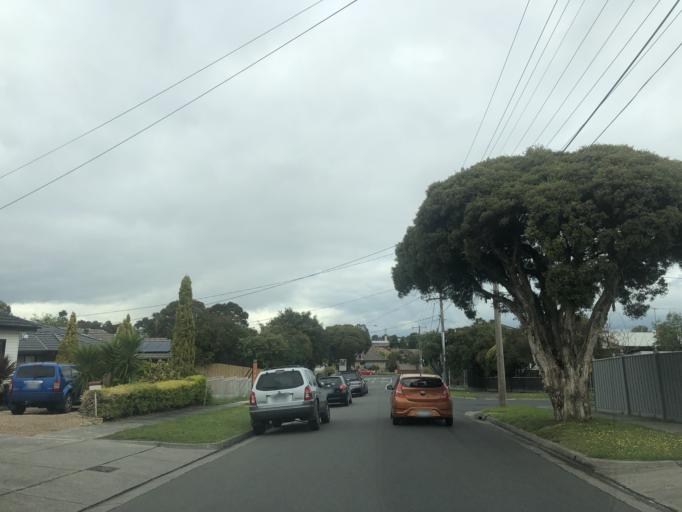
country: AU
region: Victoria
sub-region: Greater Dandenong
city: Dandenong North
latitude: -37.9691
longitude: 145.2173
